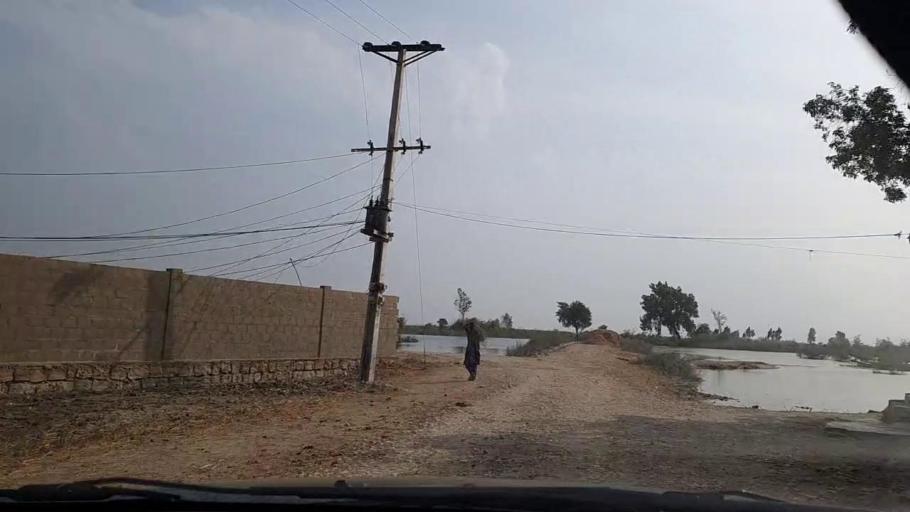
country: PK
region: Sindh
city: Thatta
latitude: 24.5822
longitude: 67.9033
